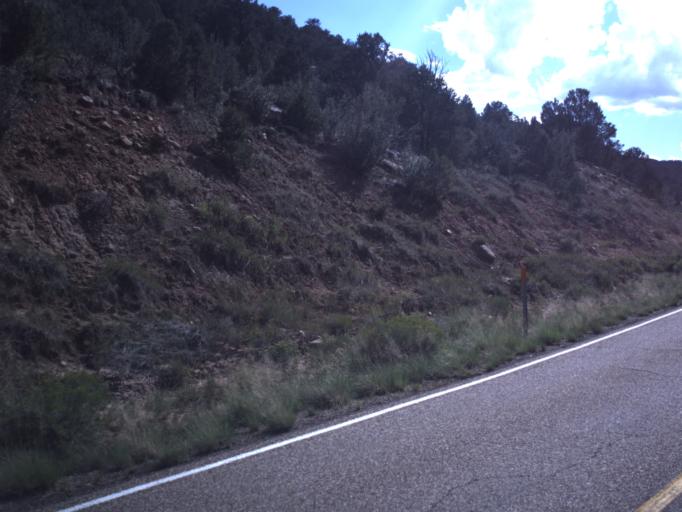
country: US
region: Utah
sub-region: Duchesne County
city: Duchesne
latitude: 40.3210
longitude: -110.6921
